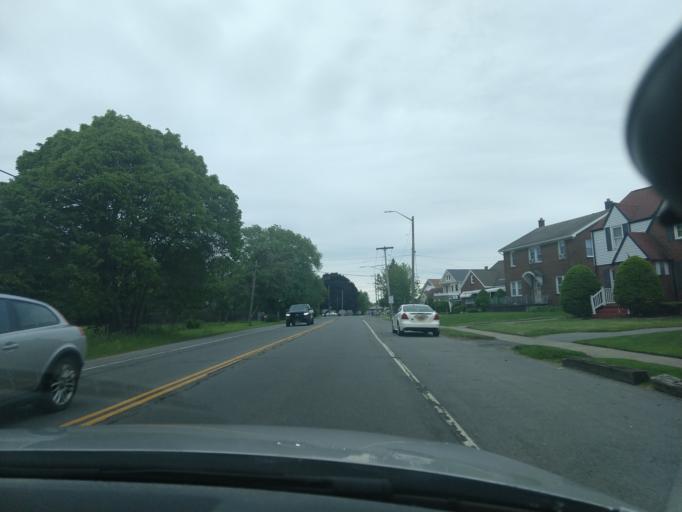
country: US
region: New York
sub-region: Erie County
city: West Seneca
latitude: 42.8387
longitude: -78.7982
